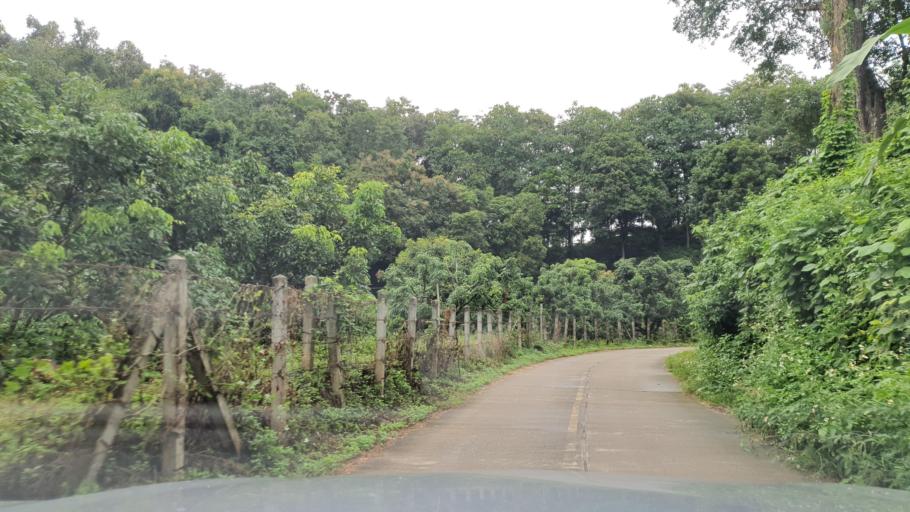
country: TH
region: Chiang Mai
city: Mae Taeng
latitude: 19.1989
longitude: 98.9393
